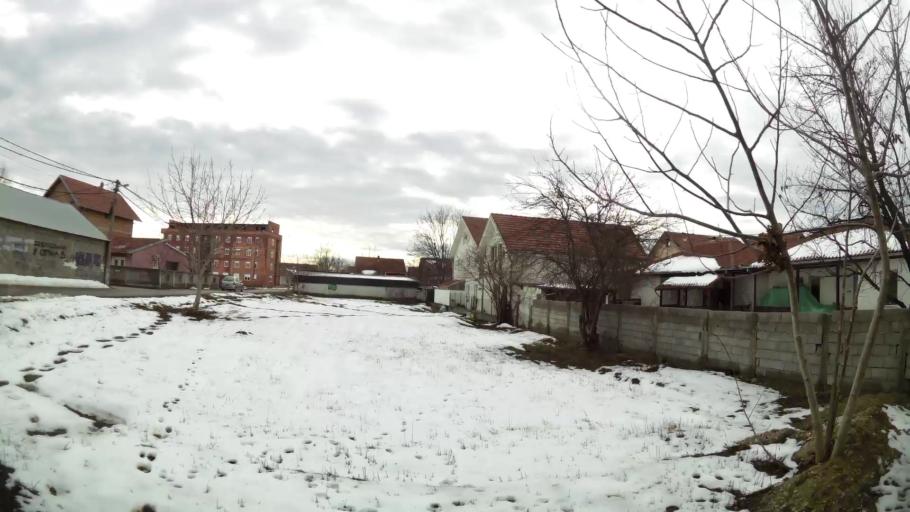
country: RS
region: Central Serbia
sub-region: Belgrade
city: Surcin
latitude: 44.8043
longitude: 20.3343
